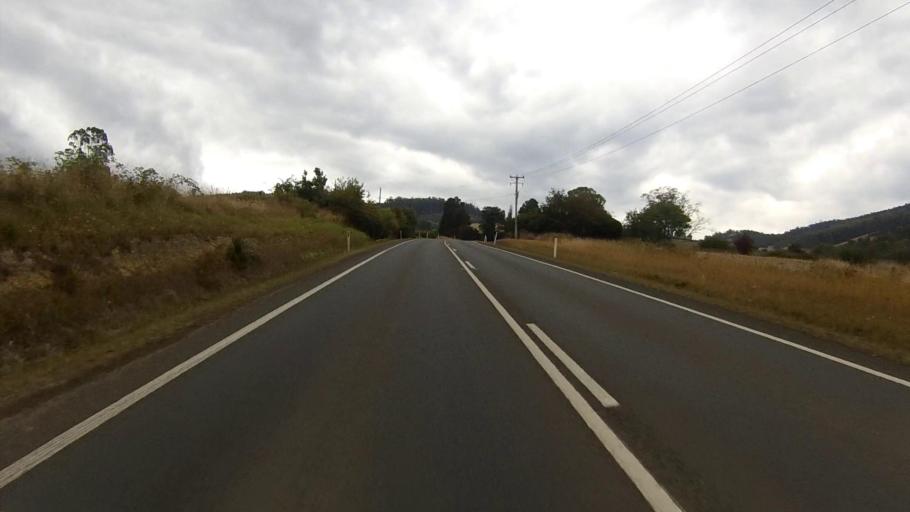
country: AU
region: Tasmania
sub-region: Huon Valley
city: Cygnet
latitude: -43.1389
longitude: 147.0586
